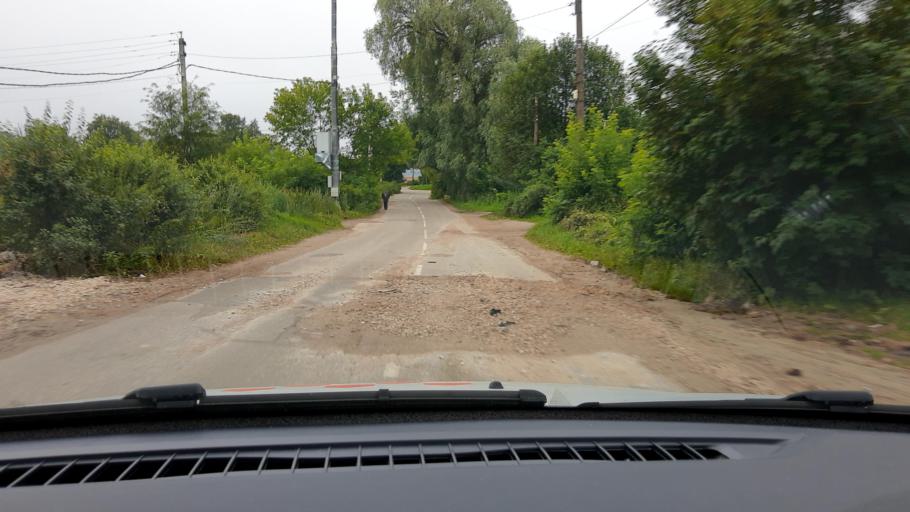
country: RU
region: Nizjnij Novgorod
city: Bogorodsk
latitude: 56.0952
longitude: 43.5122
